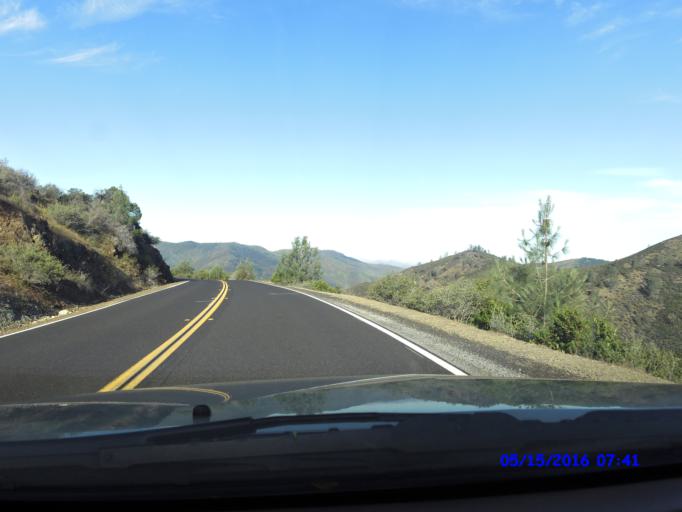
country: US
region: California
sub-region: Mariposa County
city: Mariposa
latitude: 37.6571
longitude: -120.1479
